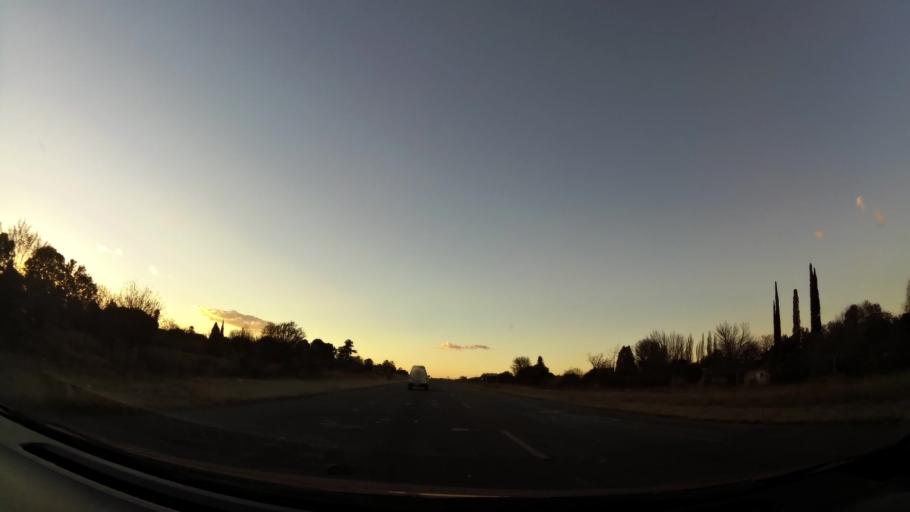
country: ZA
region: North-West
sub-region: Dr Kenneth Kaunda District Municipality
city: Potchefstroom
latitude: -26.6848
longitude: 27.0763
